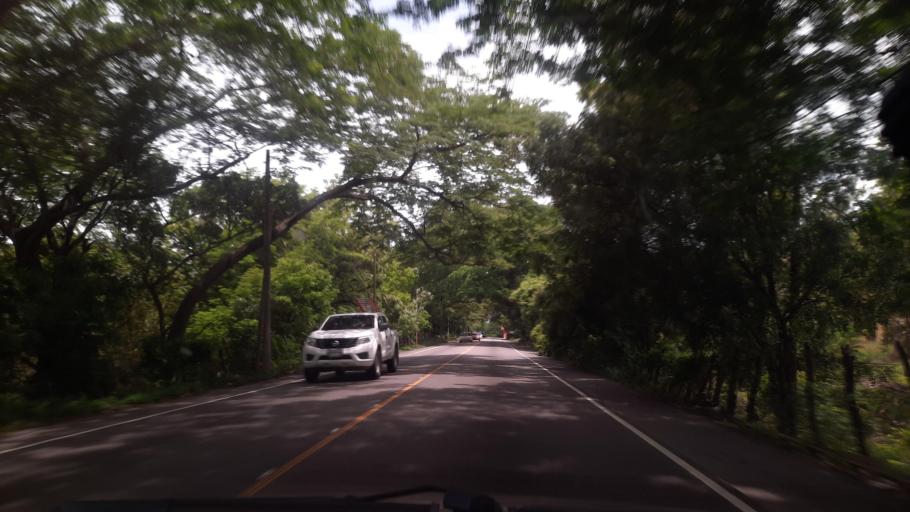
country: GT
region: Zacapa
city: Rio Hondo
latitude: 15.0647
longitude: -89.5281
